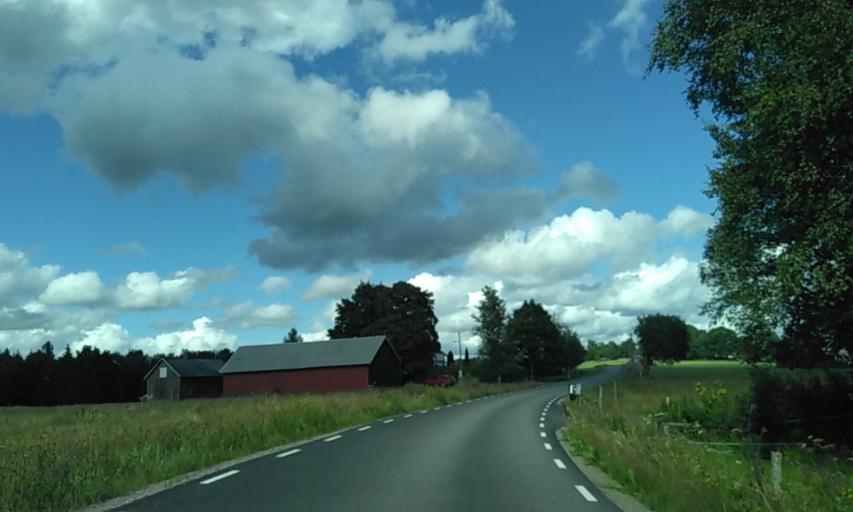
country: SE
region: Vaestra Goetaland
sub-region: Vargarda Kommun
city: Vargarda
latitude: 57.9703
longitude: 12.8996
